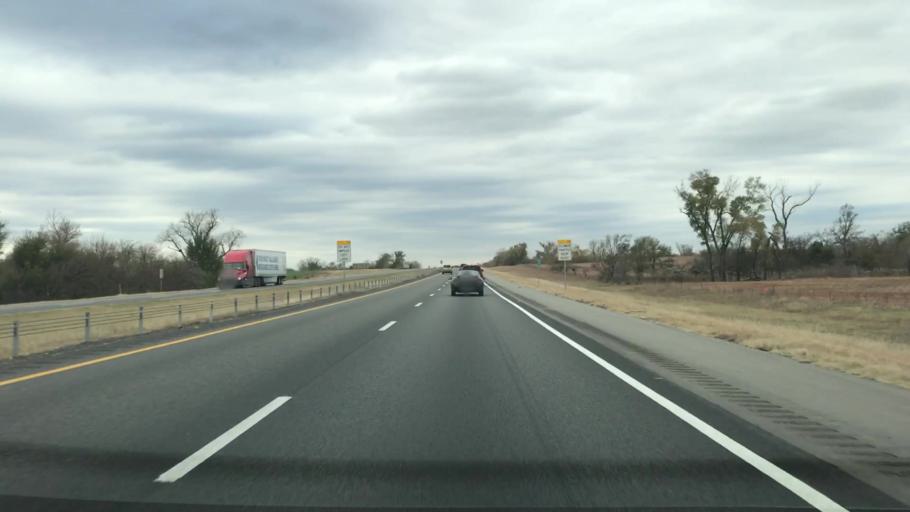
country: US
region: Oklahoma
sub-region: Beckham County
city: Elk City
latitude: 35.3859
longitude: -99.4861
